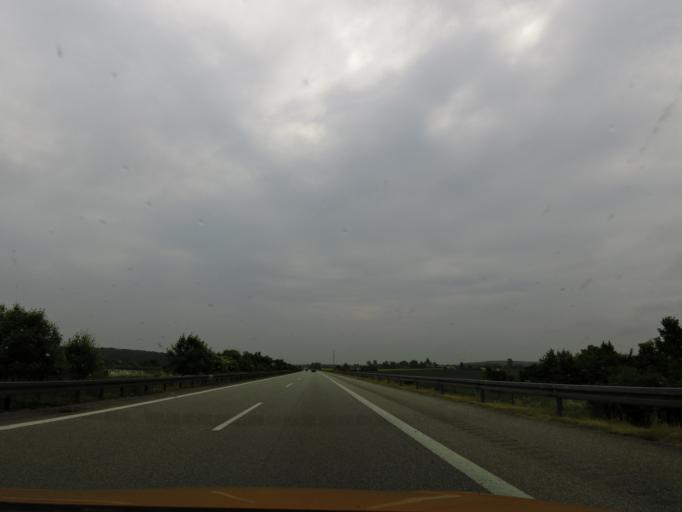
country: DE
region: Mecklenburg-Vorpommern
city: Rehna
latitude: 53.8223
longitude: 11.0815
